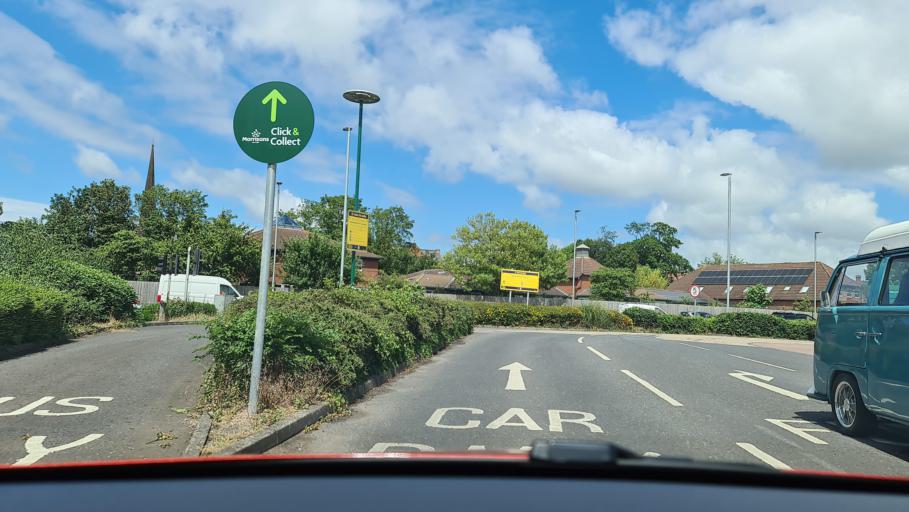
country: GB
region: England
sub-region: Somerset
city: Bridgwater
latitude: 51.1253
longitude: -3.0043
